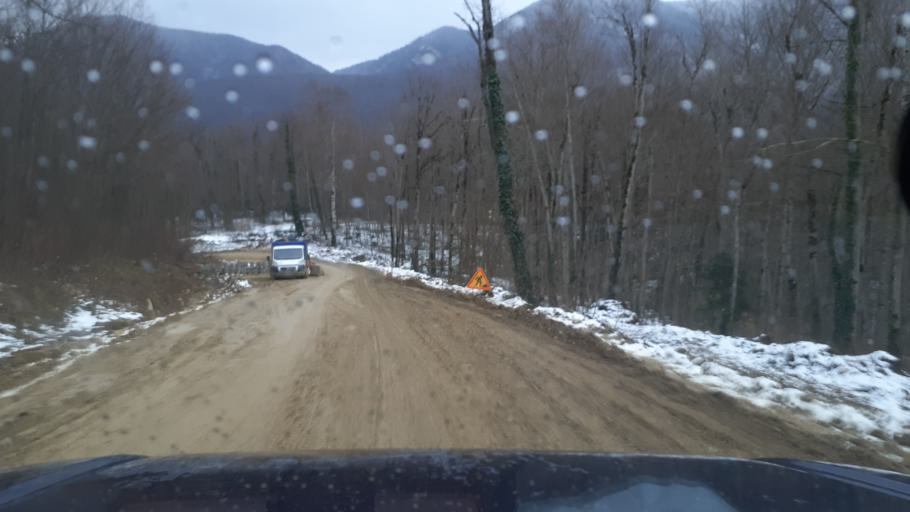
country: RU
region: Krasnodarskiy
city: Neftegorsk
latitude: 44.1634
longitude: 39.8232
